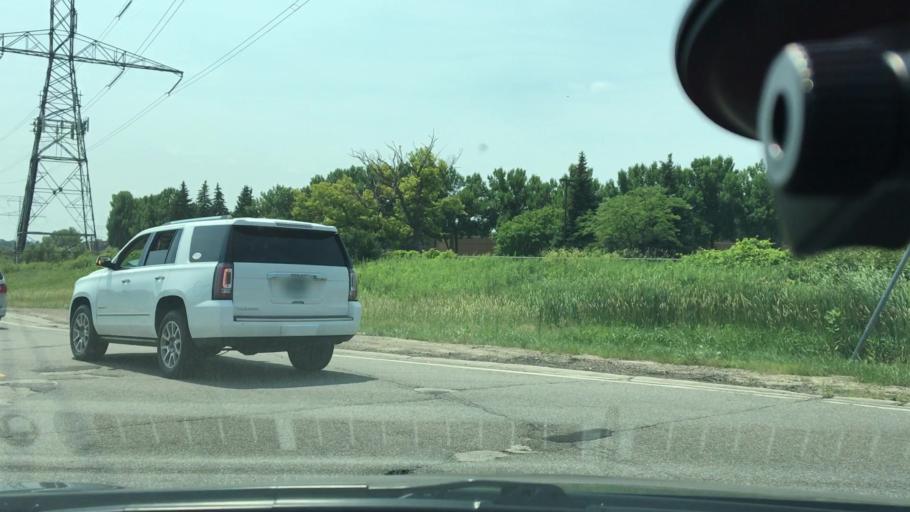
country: US
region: Minnesota
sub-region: Hennepin County
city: Plymouth
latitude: 45.0287
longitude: -93.4538
